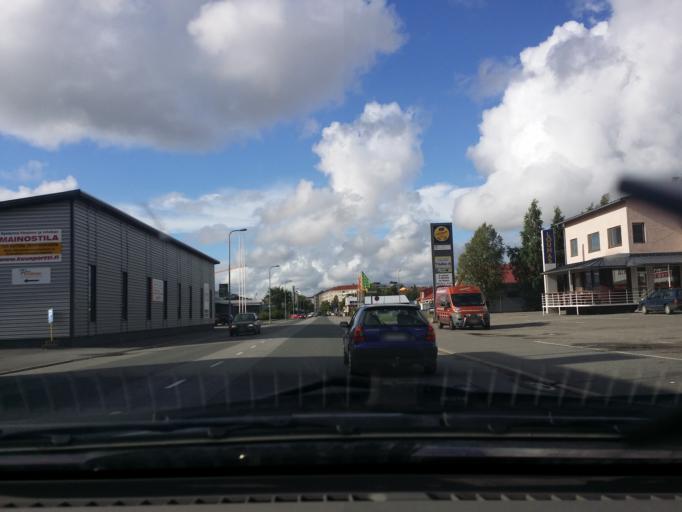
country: FI
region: Satakunta
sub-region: Pori
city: Pori
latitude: 61.4742
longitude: 21.7977
